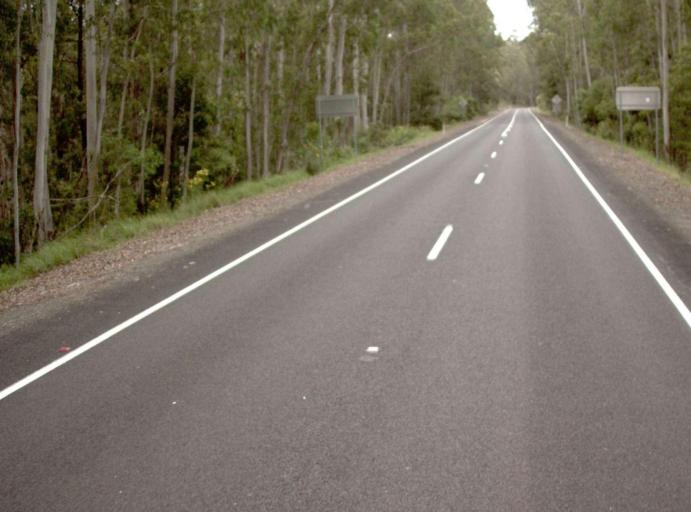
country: AU
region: New South Wales
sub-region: Bombala
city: Bombala
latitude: -37.2979
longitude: 149.2123
